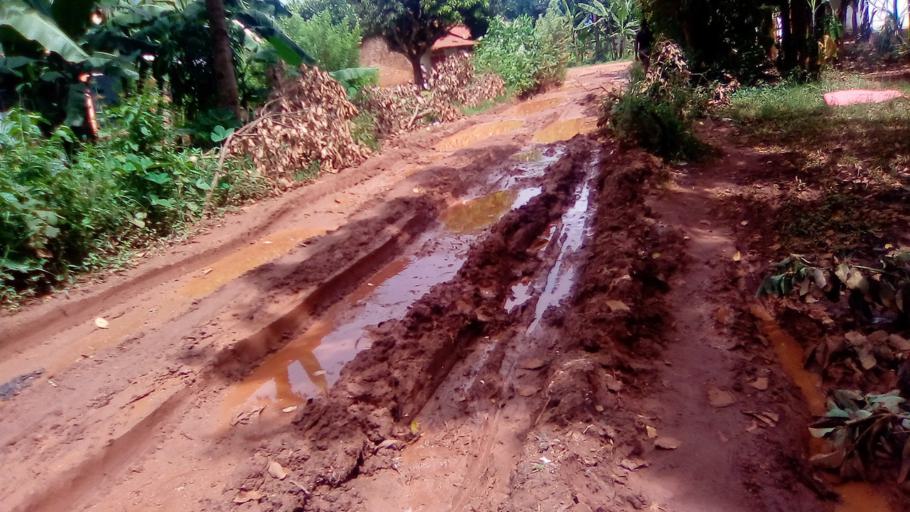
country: UG
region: Central Region
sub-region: Wakiso District
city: Entebbe
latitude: 0.1017
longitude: 32.5264
